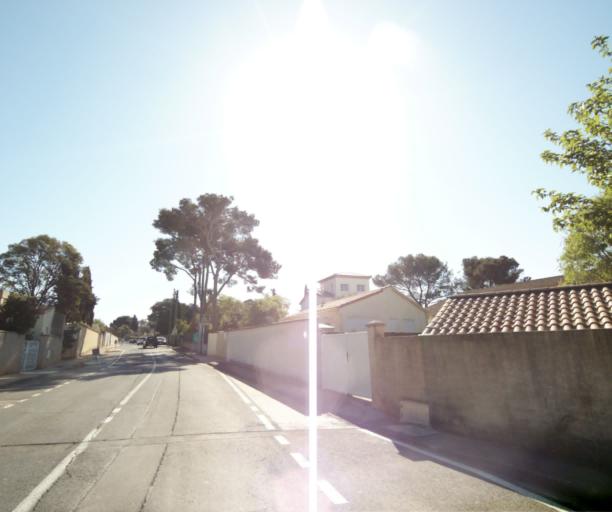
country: FR
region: Languedoc-Roussillon
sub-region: Departement de l'Herault
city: Castelnau-le-Lez
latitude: 43.6357
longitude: 3.9137
